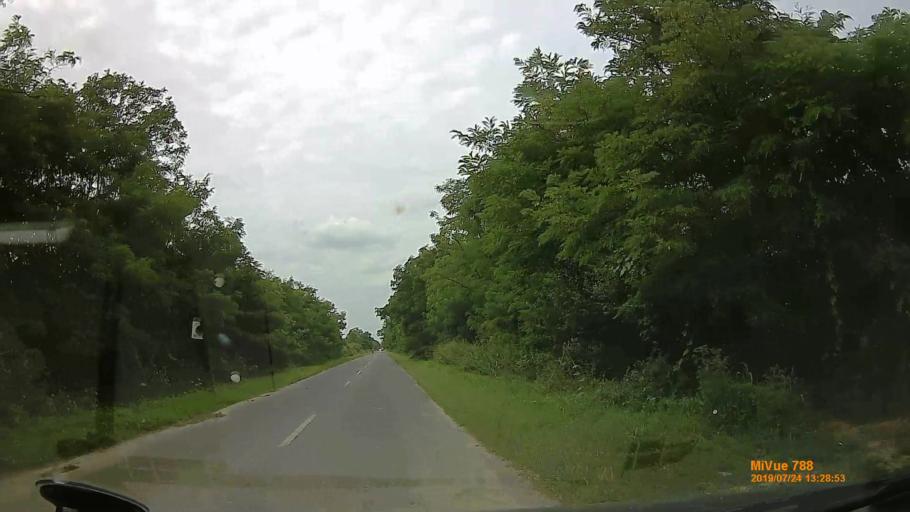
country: UA
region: Zakarpattia
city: Batiovo
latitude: 48.2243
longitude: 22.4094
